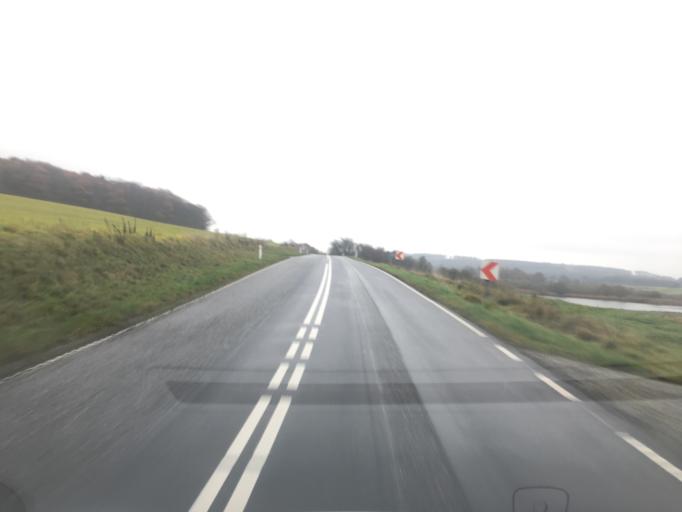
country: DK
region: Central Jutland
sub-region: Randers Kommune
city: Assentoft
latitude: 56.3945
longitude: 10.1602
